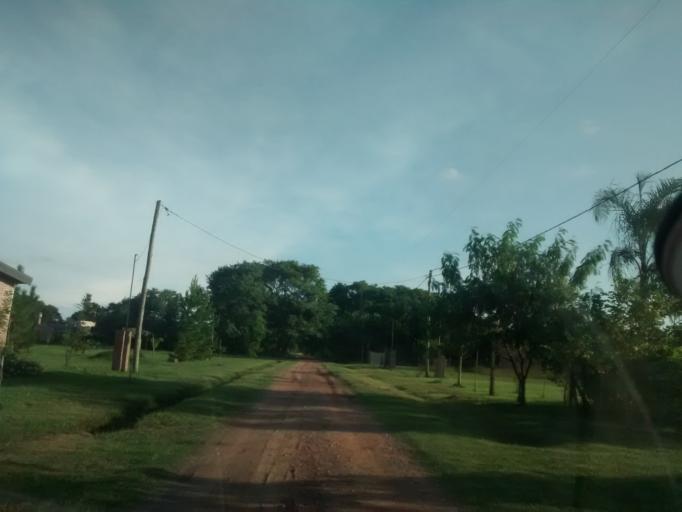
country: AR
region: Chaco
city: Colonia Benitez
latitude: -27.3082
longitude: -58.9905
